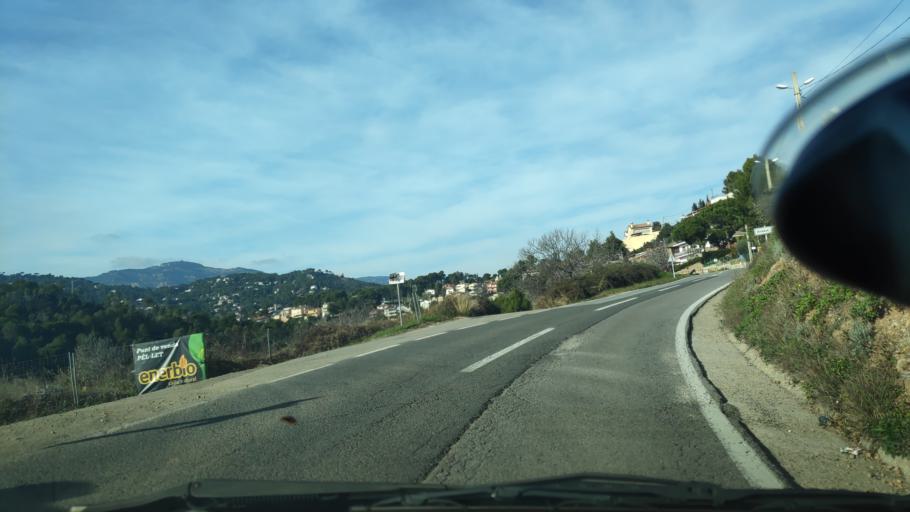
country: ES
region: Catalonia
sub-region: Provincia de Barcelona
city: Castellar del Valles
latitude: 41.6171
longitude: 2.0813
